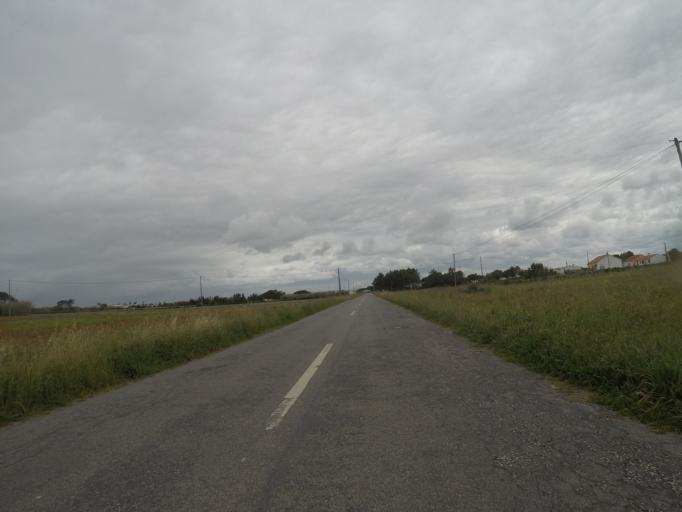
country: PT
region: Beja
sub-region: Odemira
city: Vila Nova de Milfontes
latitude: 37.6113
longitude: -8.7935
